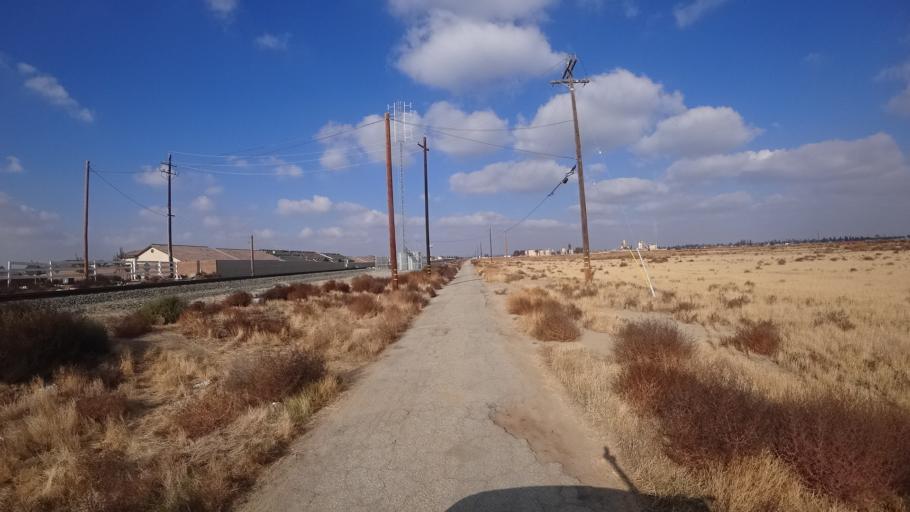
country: US
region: California
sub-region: Kern County
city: Greenacres
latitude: 35.2888
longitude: -119.1010
